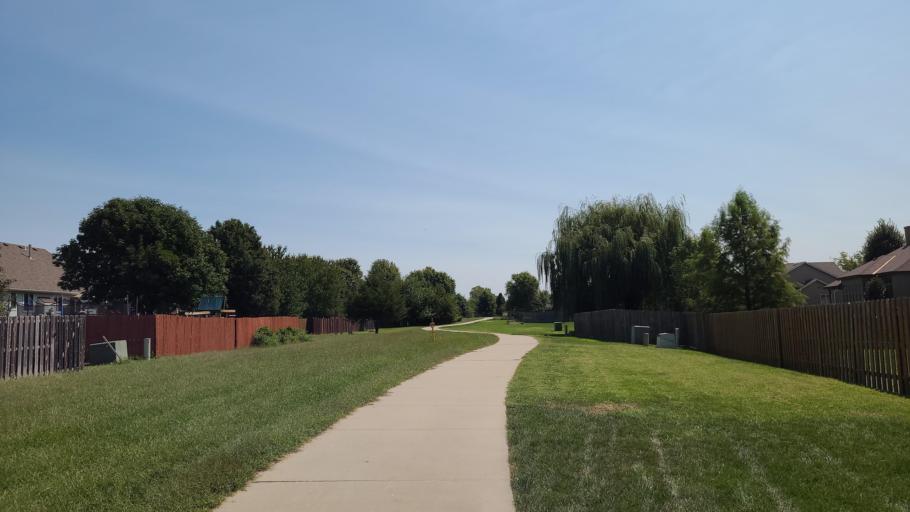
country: US
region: Kansas
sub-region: Douglas County
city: Lawrence
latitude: 38.9662
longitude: -95.3200
